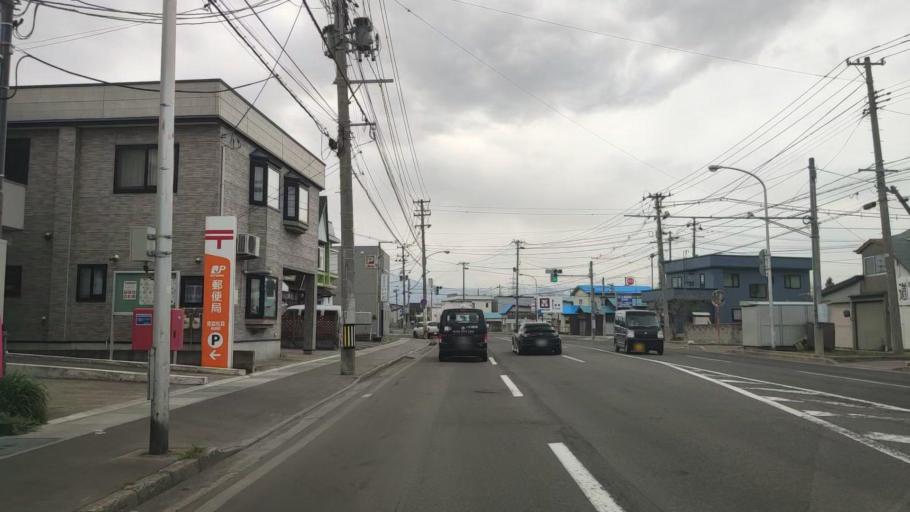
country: JP
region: Aomori
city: Aomori Shi
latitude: 40.8140
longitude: 140.7762
